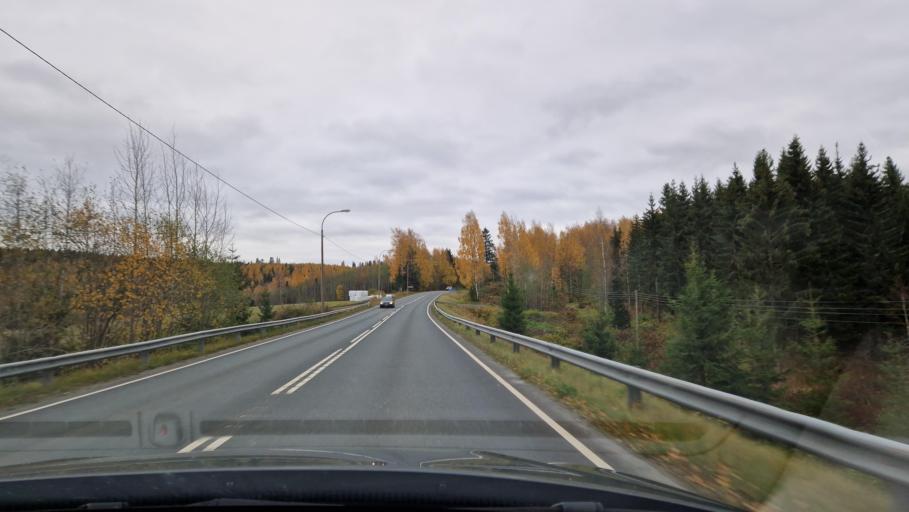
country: FI
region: Northern Savo
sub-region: Kuopio
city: Nilsiae
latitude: 63.1359
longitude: 27.9752
